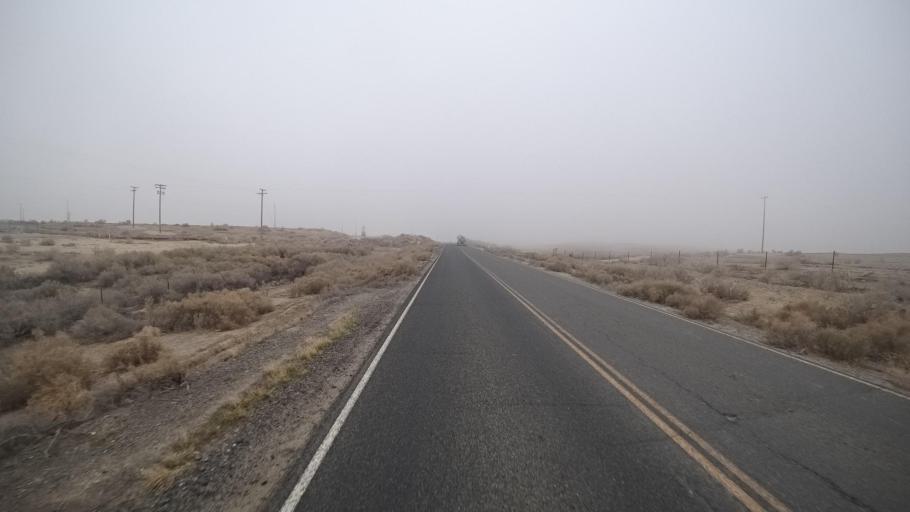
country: US
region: California
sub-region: Kern County
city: Ford City
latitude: 35.2737
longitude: -119.4675
